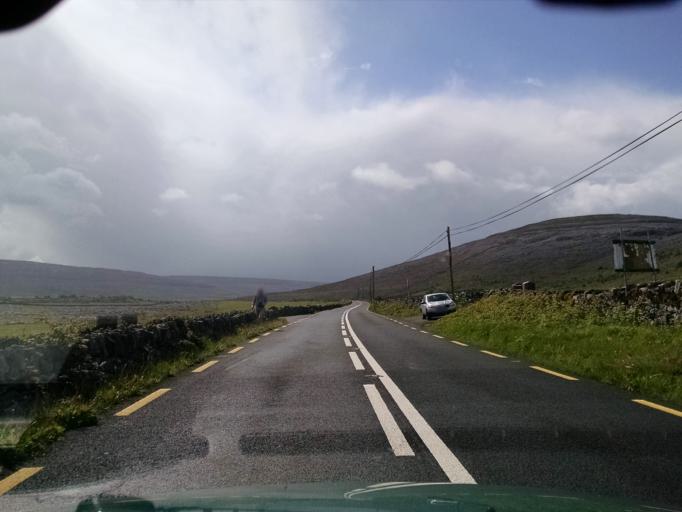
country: IE
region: Connaught
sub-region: County Galway
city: Bearna
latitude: 53.1358
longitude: -9.0994
